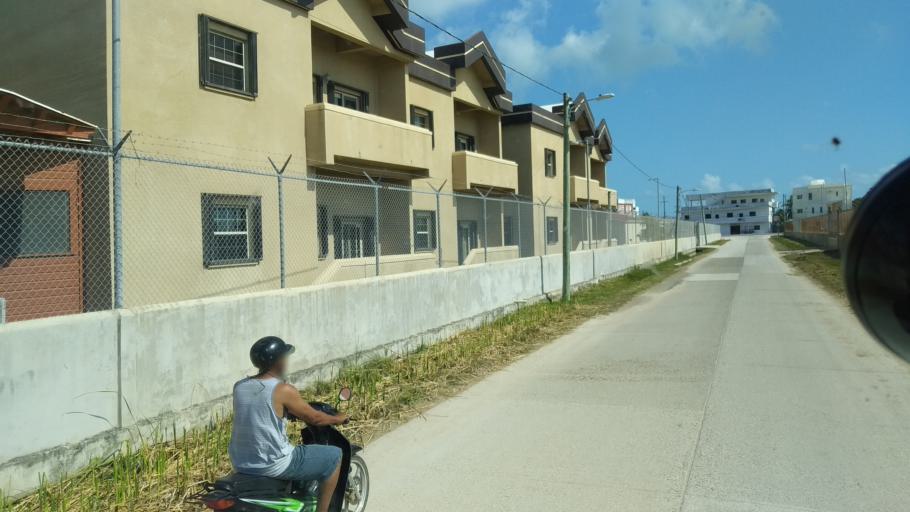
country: BZ
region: Belize
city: Belize City
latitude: 17.5143
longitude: -88.2276
